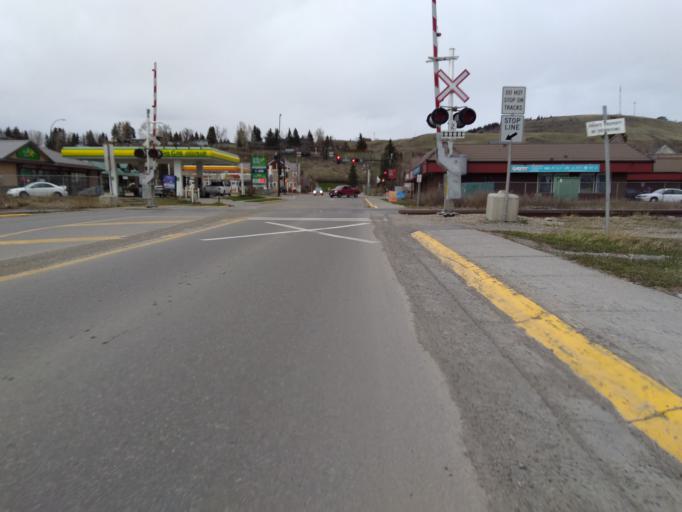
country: CA
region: Alberta
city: Cochrane
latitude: 51.1911
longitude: -114.4739
